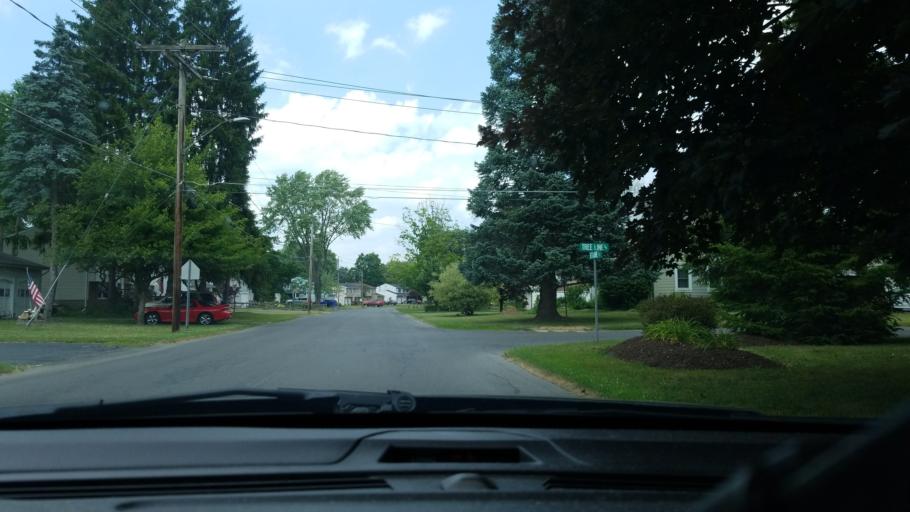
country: US
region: New York
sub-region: Onondaga County
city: Liverpool
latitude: 43.1408
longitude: -76.2110
